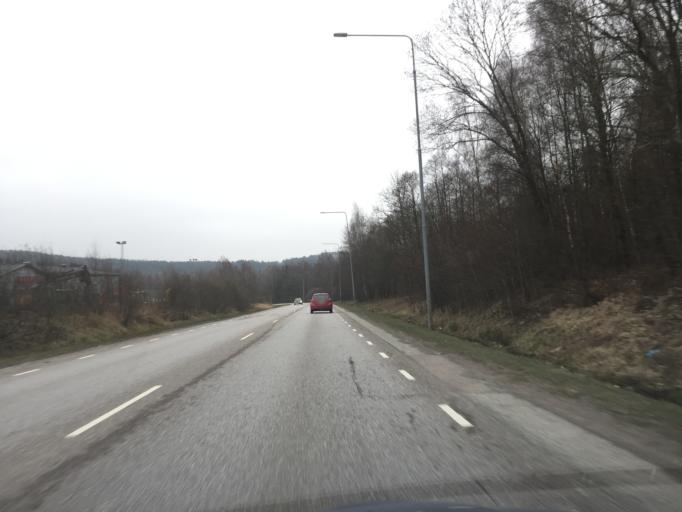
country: SE
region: Vaestra Goetaland
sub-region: Goteborg
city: Eriksbo
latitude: 57.7773
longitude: 12.0482
